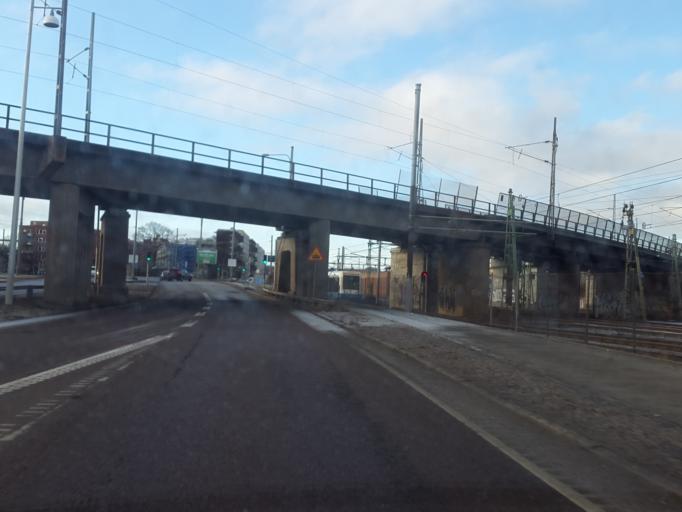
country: SE
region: Vaestra Goetaland
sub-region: Goteborg
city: Goeteborg
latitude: 57.7142
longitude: 11.9921
